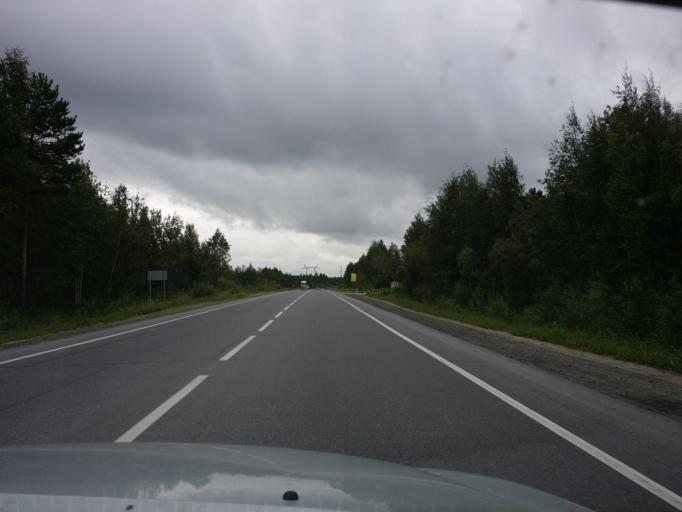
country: RU
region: Khanty-Mansiyskiy Avtonomnyy Okrug
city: Megion
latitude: 61.0514
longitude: 76.3287
